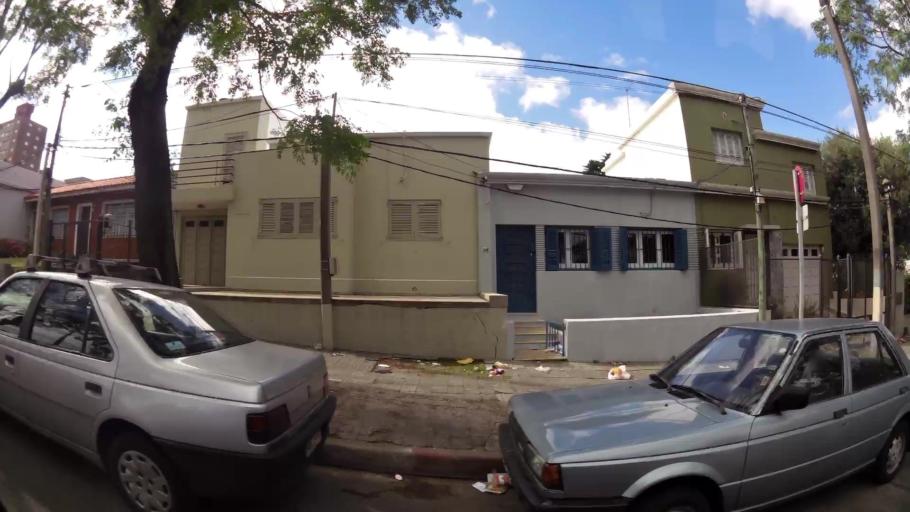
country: UY
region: Montevideo
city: Montevideo
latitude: -34.8886
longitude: -56.1302
